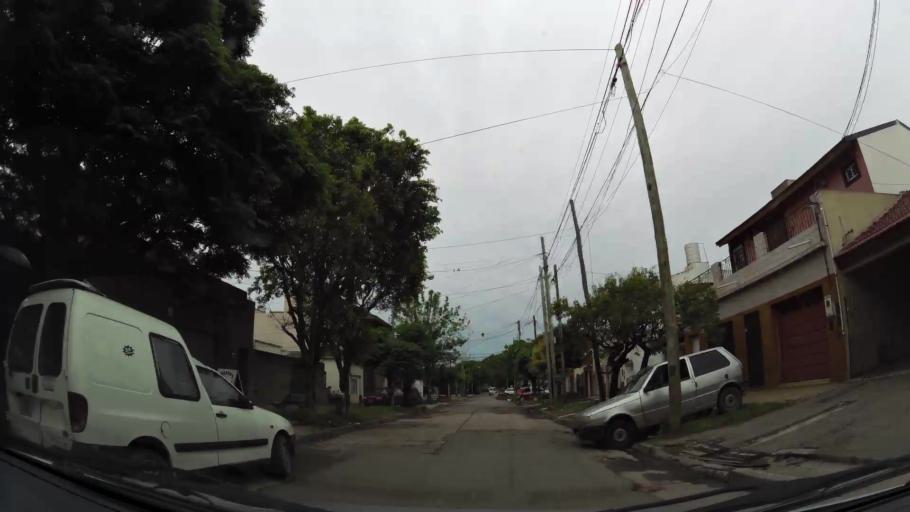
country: AR
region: Buenos Aires
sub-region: Partido de Lanus
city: Lanus
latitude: -34.7172
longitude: -58.3619
